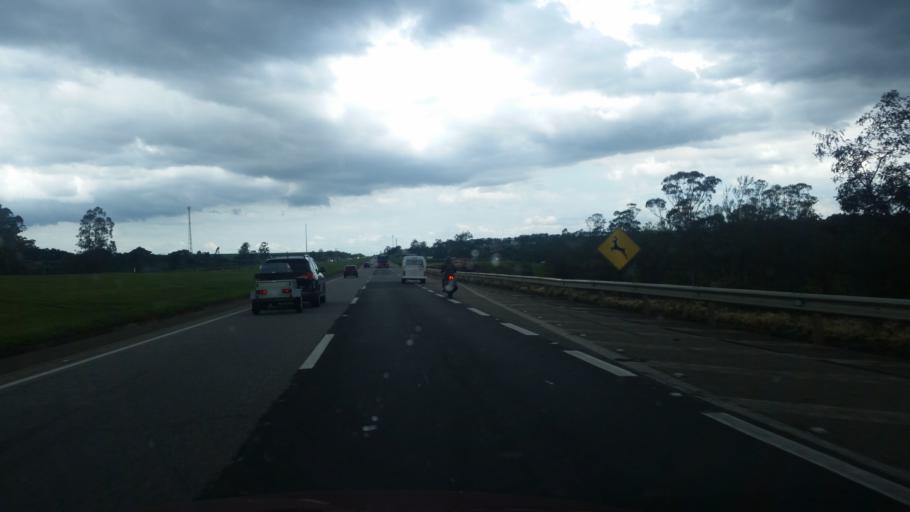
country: BR
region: Sao Paulo
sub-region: Porto Feliz
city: Porto Feliz
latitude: -23.3421
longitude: -47.5344
